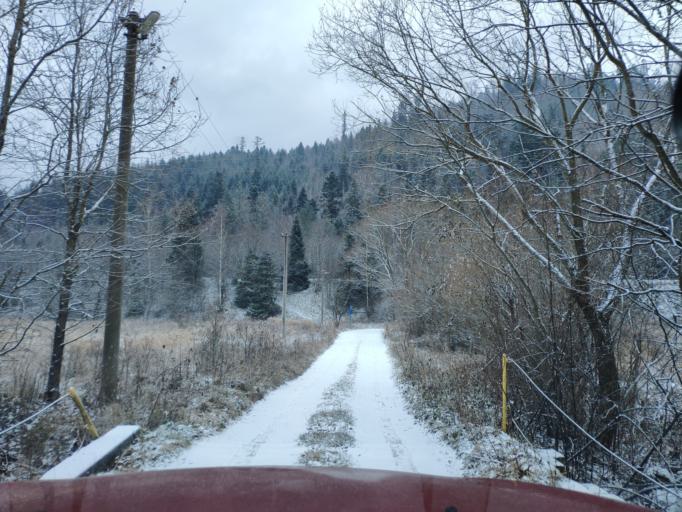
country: SK
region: Kosicky
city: Spisska Nova Ves
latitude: 48.8169
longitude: 20.5435
